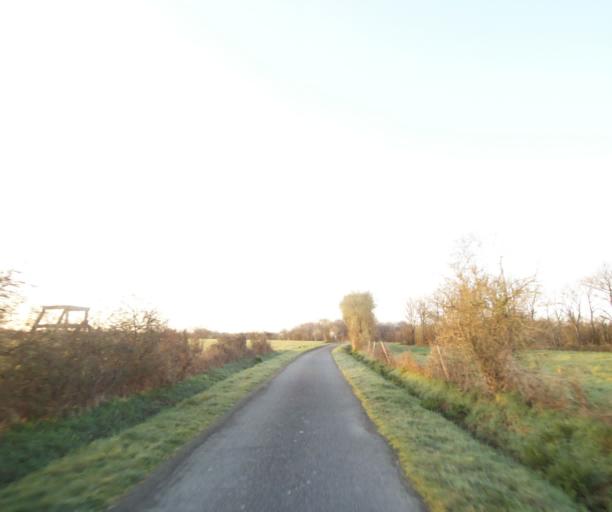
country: FR
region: Pays de la Loire
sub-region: Departement de la Loire-Atlantique
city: Quilly
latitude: 47.4406
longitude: -1.9040
